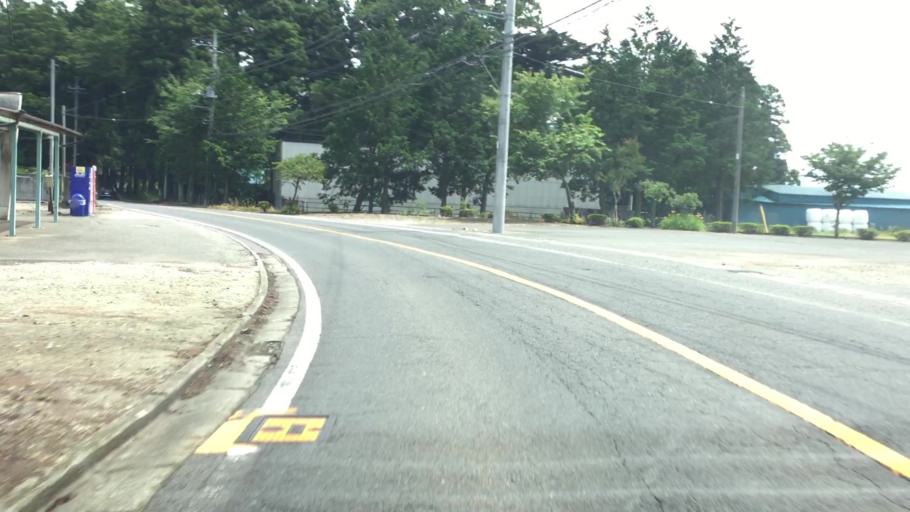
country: JP
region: Tochigi
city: Kuroiso
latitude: 37.0359
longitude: 139.9421
